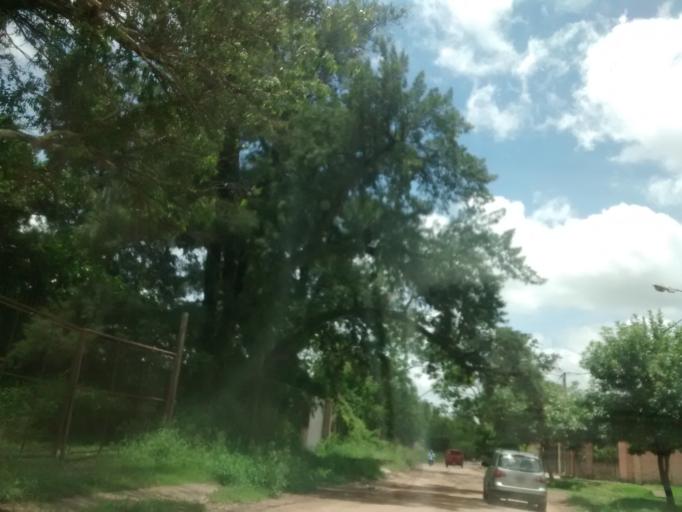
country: AR
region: Chaco
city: Fontana
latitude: -27.4273
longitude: -59.0082
